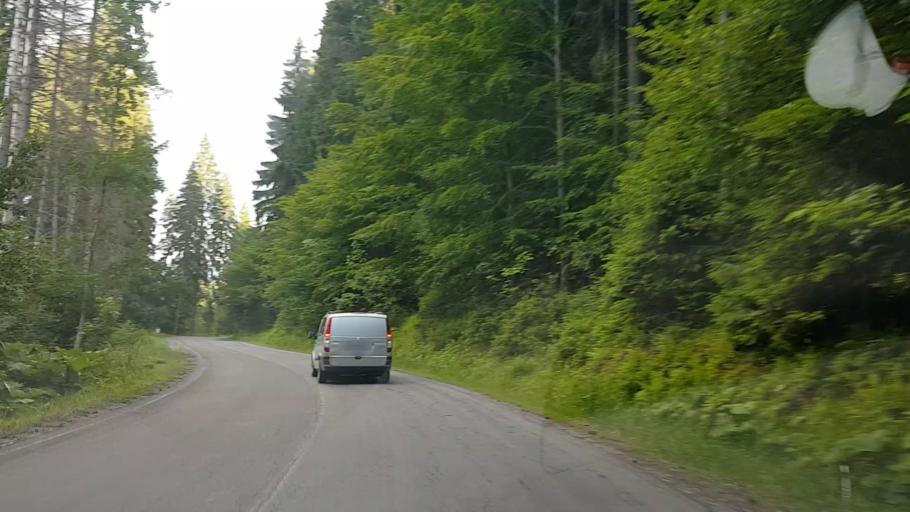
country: RO
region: Harghita
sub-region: Comuna Varsag
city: Varsag
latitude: 46.6676
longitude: 25.3190
